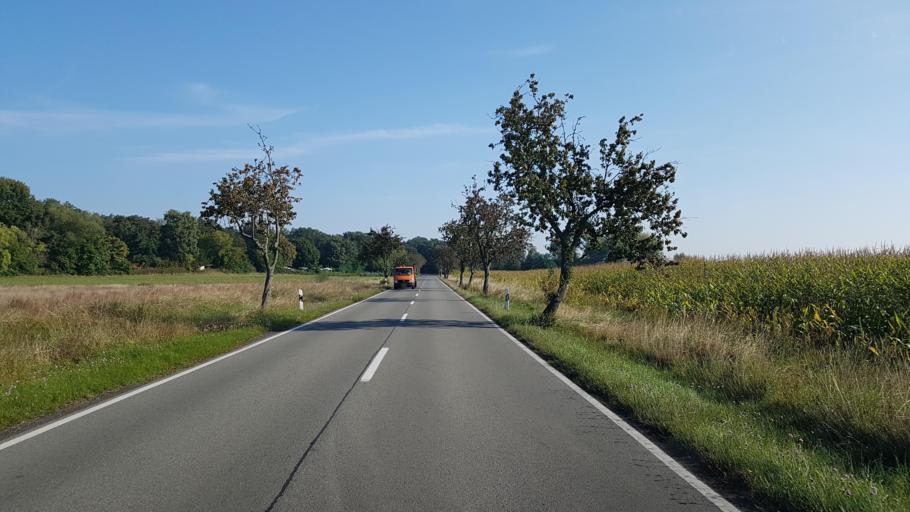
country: DE
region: Brandenburg
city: Brandenburg an der Havel
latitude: 52.4830
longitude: 12.5954
